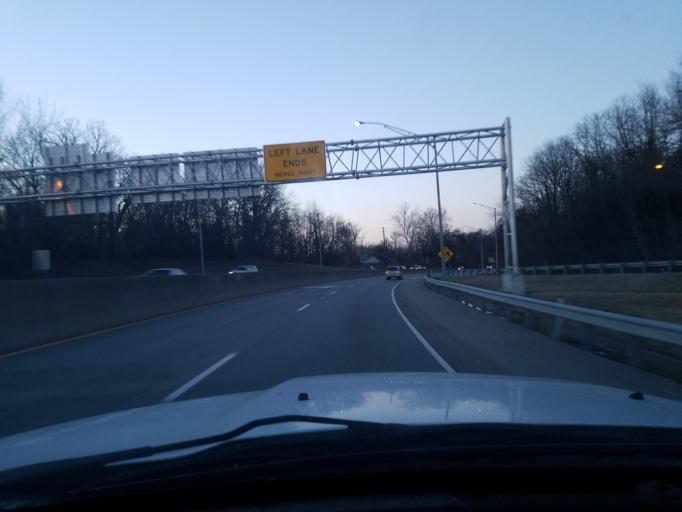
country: US
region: Kentucky
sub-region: Henderson County
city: Henderson
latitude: 37.8587
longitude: -87.5747
